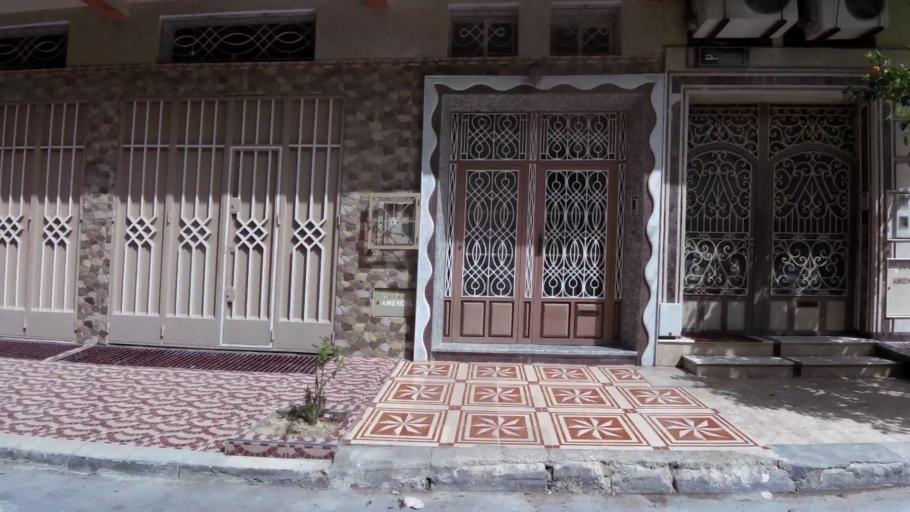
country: MA
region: Tanger-Tetouan
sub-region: Tanger-Assilah
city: Tangier
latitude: 35.7425
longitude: -5.8325
